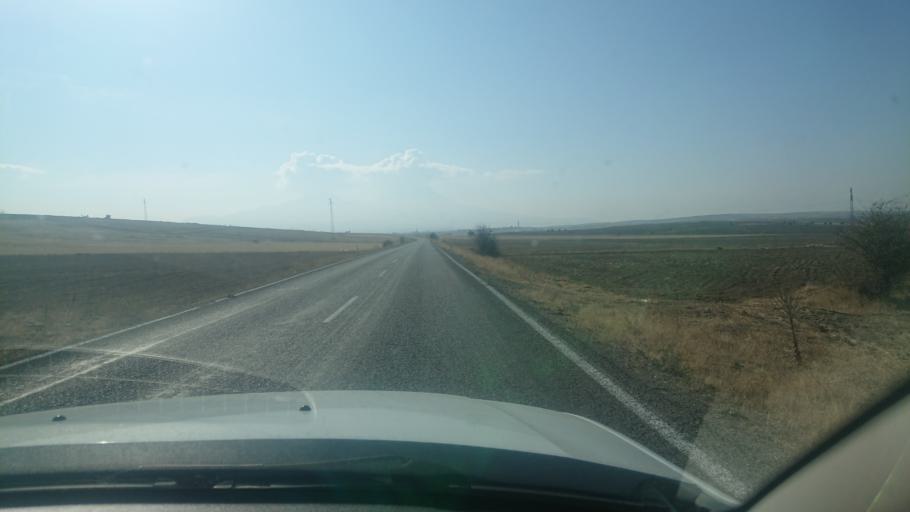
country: TR
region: Aksaray
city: Guzelyurt
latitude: 38.3024
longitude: 34.3206
